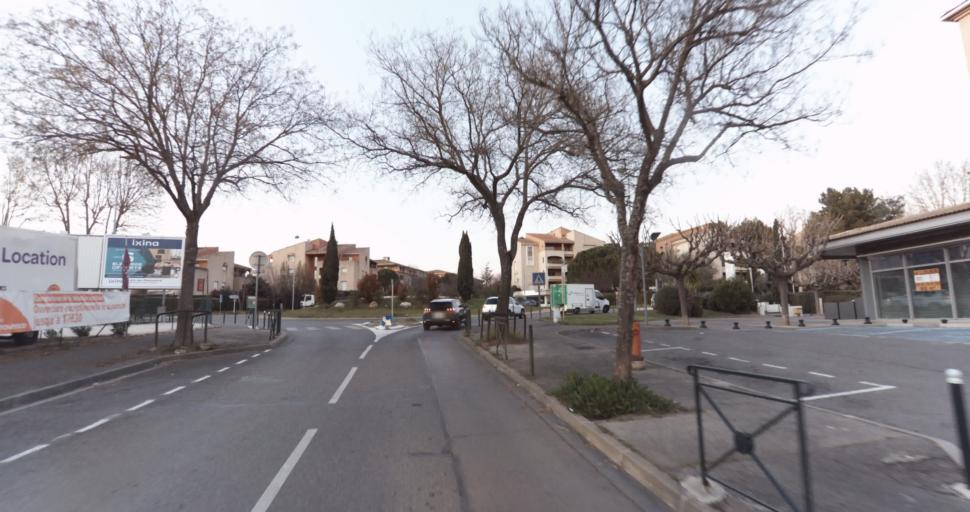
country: FR
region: Provence-Alpes-Cote d'Azur
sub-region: Departement des Bouches-du-Rhone
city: Aix-en-Provence
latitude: 43.5348
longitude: 5.4084
